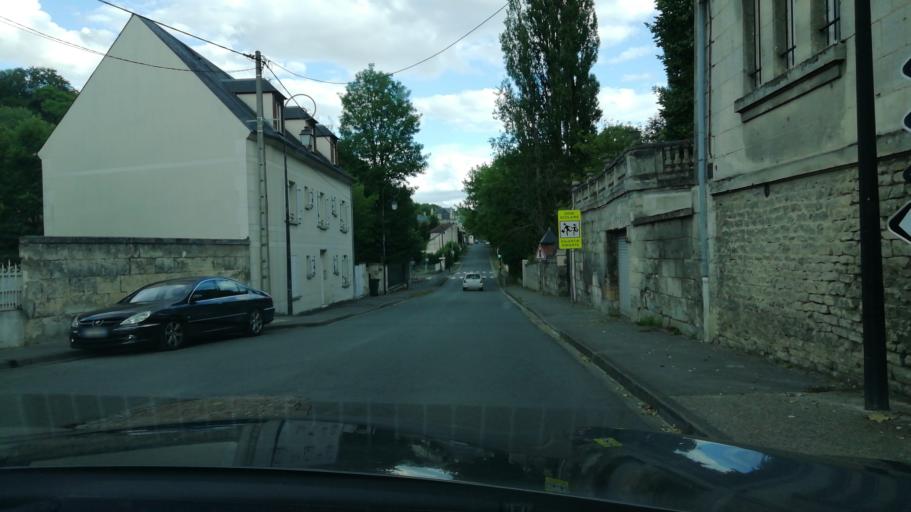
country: FR
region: Picardie
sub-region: Departement de l'Oise
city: Pierrefonds
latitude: 49.3509
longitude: 2.9811
